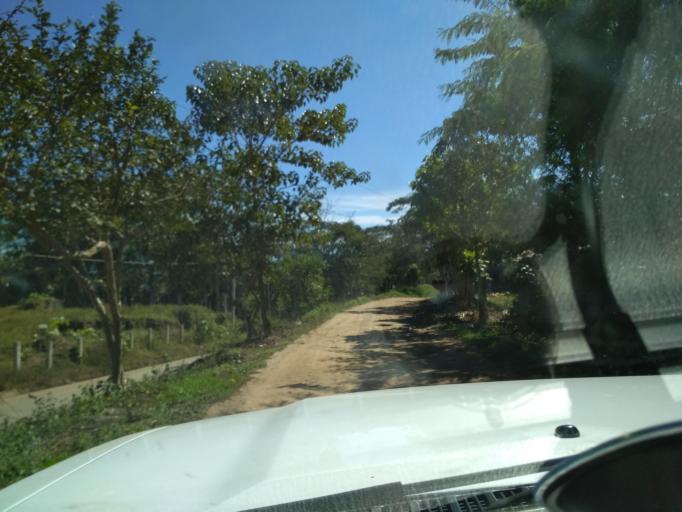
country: MX
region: Veracruz
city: El Castillo
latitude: 19.5497
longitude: -96.8522
